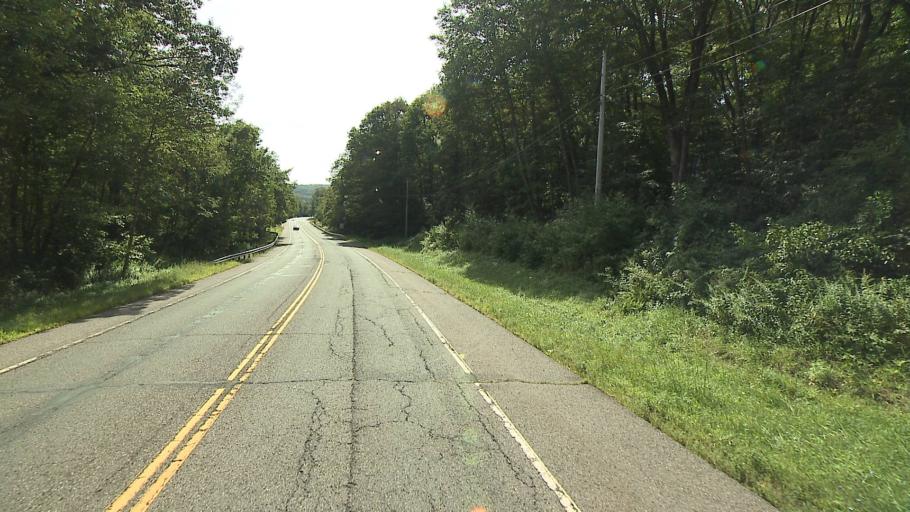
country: US
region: Connecticut
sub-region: Litchfield County
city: Thomaston
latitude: 41.6750
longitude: -73.0897
